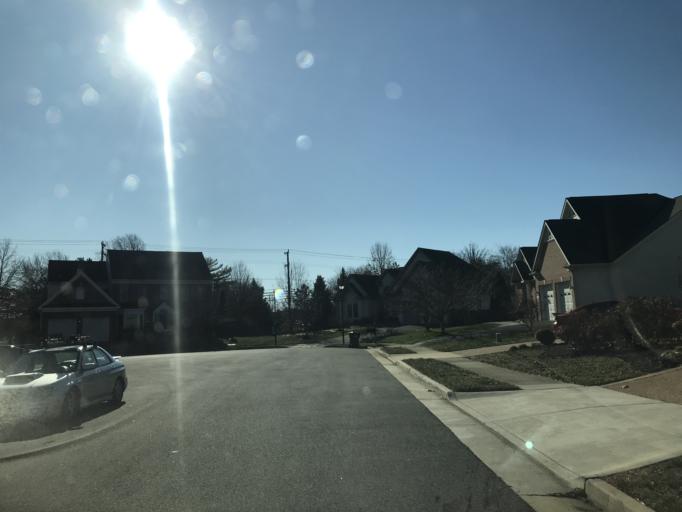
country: US
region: Virginia
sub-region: Fairfax County
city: Franconia
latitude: 38.7805
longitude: -77.1597
